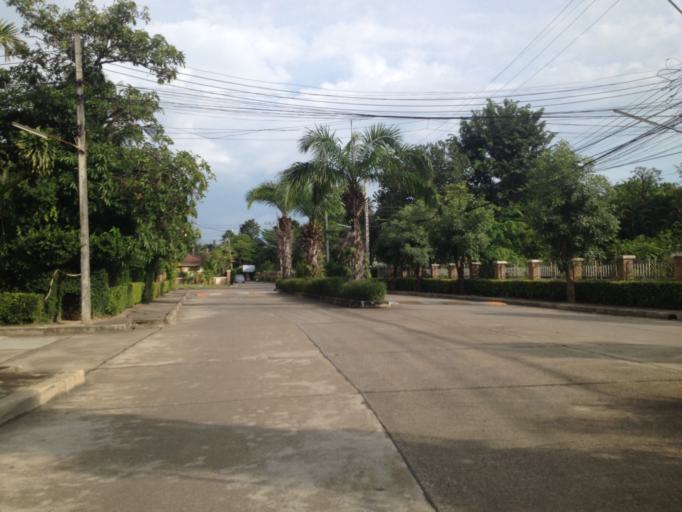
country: TH
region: Chiang Mai
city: Hang Dong
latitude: 18.7142
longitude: 98.9233
